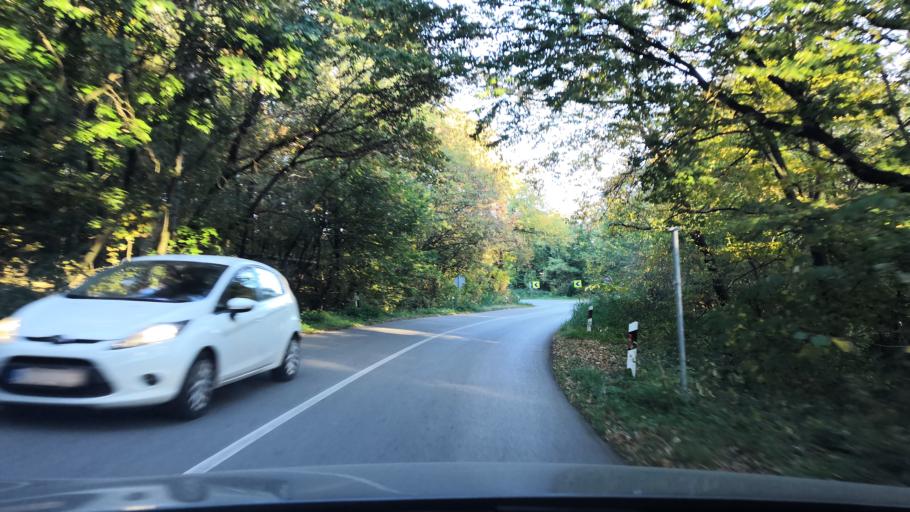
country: RS
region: Autonomna Pokrajina Vojvodina
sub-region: Sremski Okrug
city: Irig
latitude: 45.1539
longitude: 19.8470
